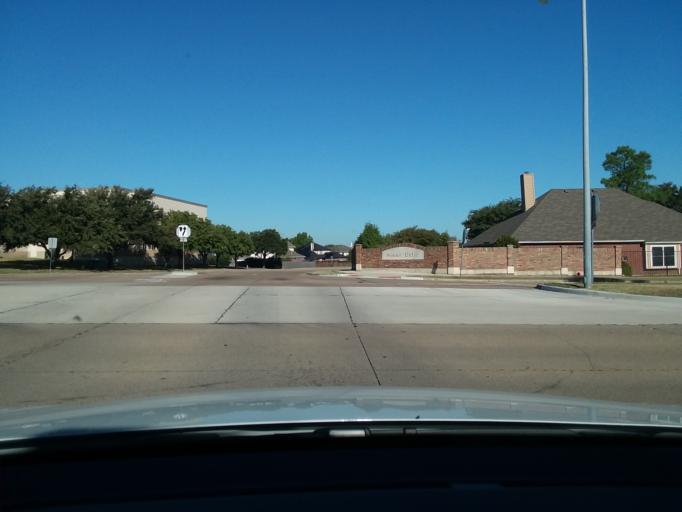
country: US
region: Texas
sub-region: Denton County
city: Lewisville
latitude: 33.0508
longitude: -97.0177
